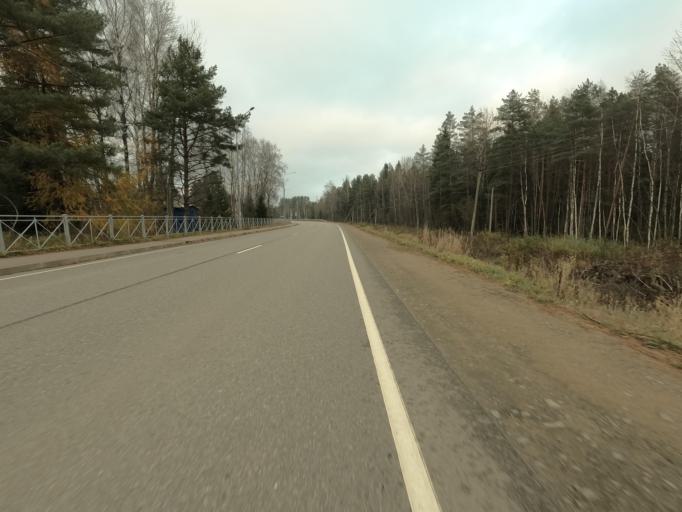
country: RU
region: Leningrad
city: Pavlovo
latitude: 59.8042
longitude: 30.9561
